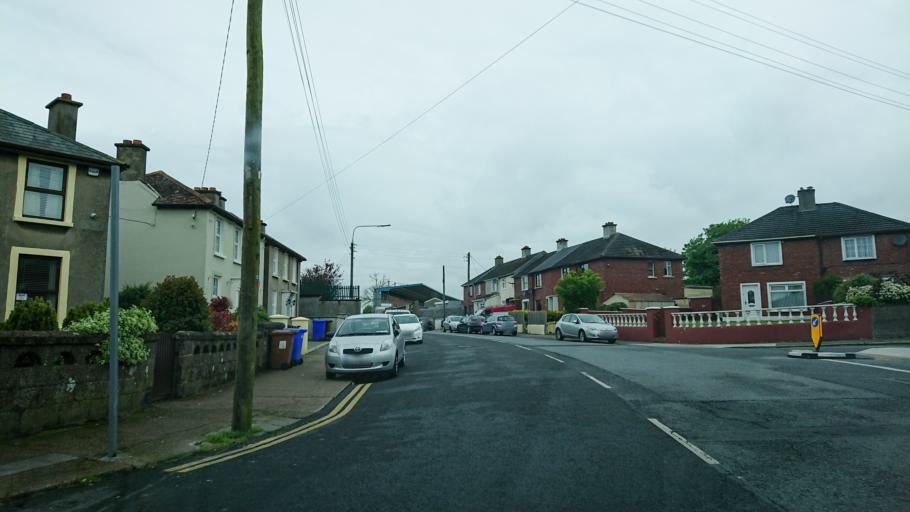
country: IE
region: Munster
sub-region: Waterford
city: Waterford
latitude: 52.2549
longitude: -7.1256
